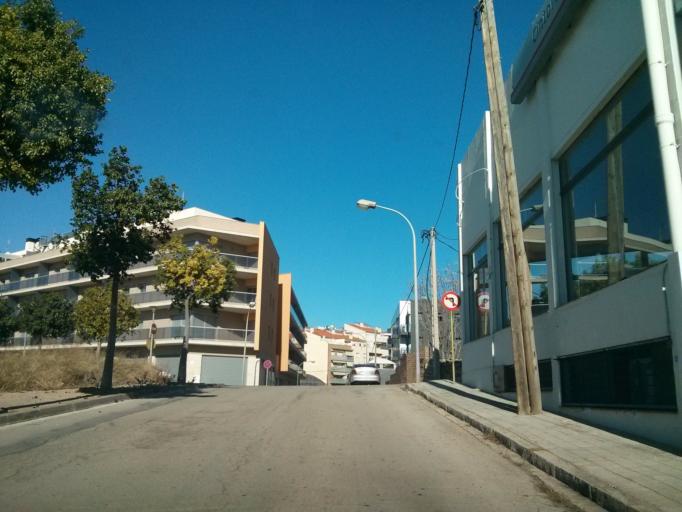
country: ES
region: Catalonia
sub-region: Provincia de Tarragona
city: El Vendrell
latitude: 41.2129
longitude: 1.5342
